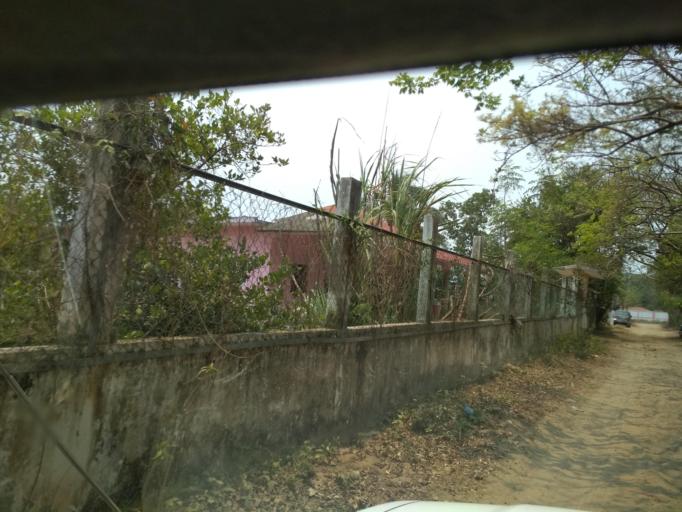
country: MX
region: Veracruz
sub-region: Veracruz
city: Delfino Victoria (Santa Fe)
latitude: 19.2115
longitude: -96.2676
